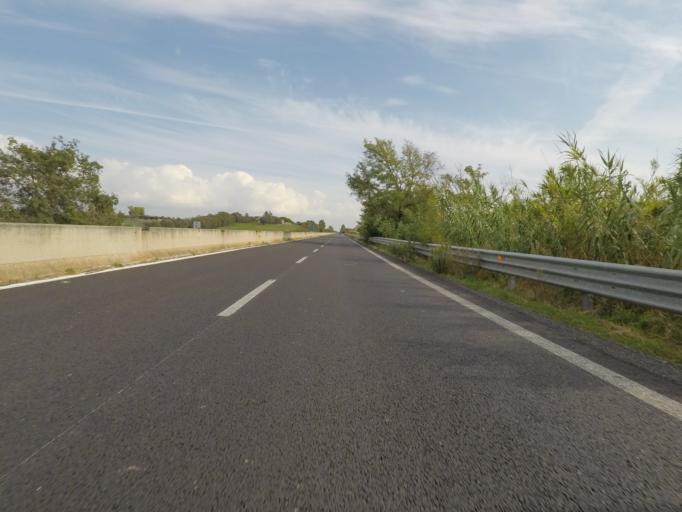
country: IT
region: Latium
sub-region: Provincia di Viterbo
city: Pescia Romana
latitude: 42.4013
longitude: 11.5031
